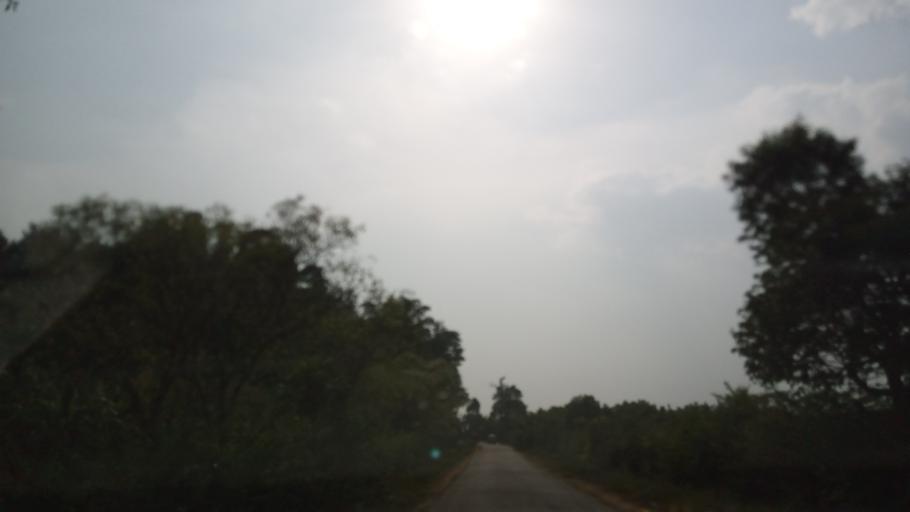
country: IN
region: Karnataka
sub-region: Chikmagalur
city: Mudigere
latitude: 13.0607
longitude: 75.6739
